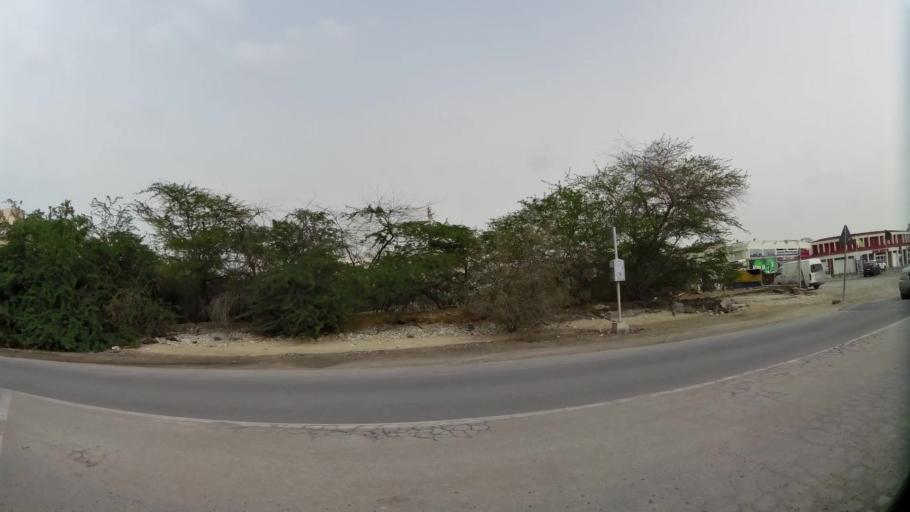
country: QA
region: Baladiyat ad Dawhah
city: Doha
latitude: 25.2521
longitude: 51.5310
